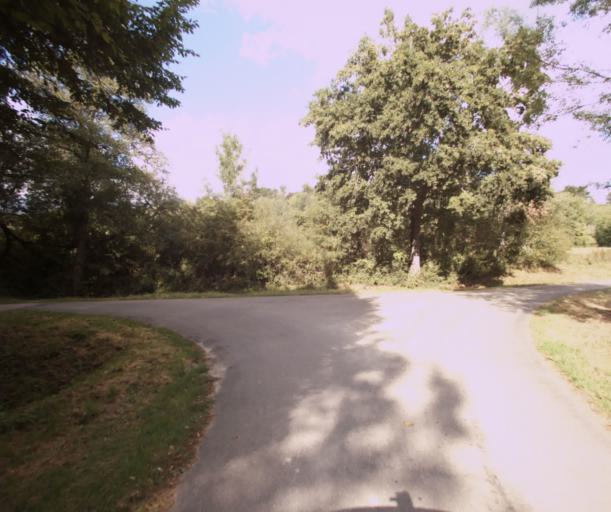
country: FR
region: Midi-Pyrenees
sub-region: Departement du Gers
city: Cazaubon
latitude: 43.9161
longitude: -0.0496
